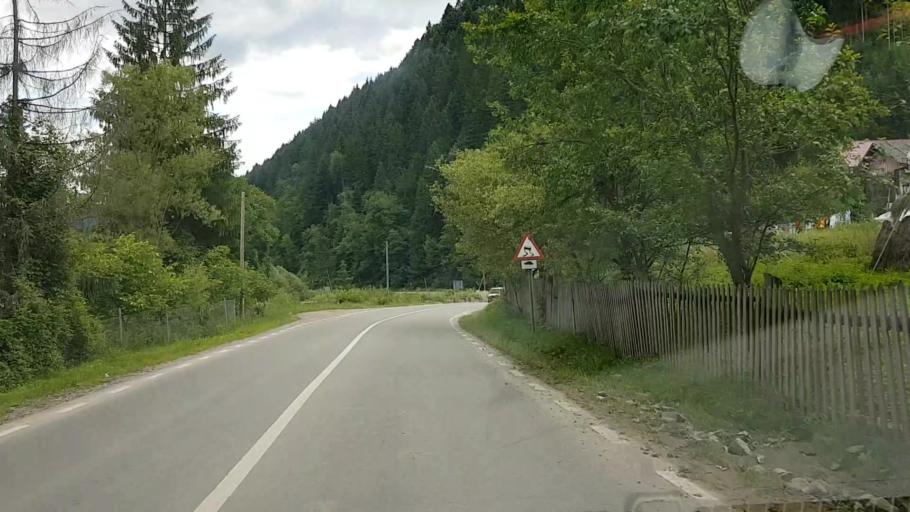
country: RO
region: Neamt
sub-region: Comuna Poiana Teiului
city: Poiana Teiului
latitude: 47.0943
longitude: 25.9451
